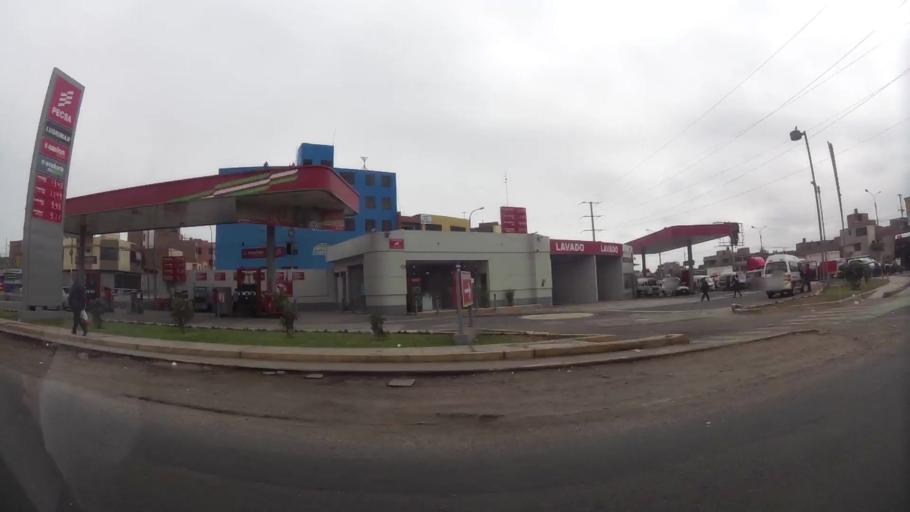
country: PE
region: Lima
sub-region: Lima
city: Independencia
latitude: -12.0070
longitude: -77.0824
